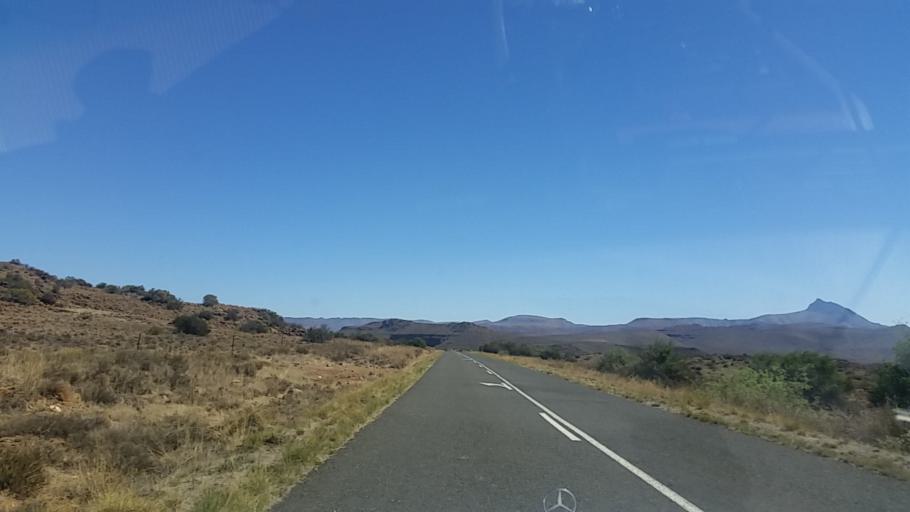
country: ZA
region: Eastern Cape
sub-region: Cacadu District Municipality
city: Graaff-Reinet
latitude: -31.8993
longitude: 24.5879
